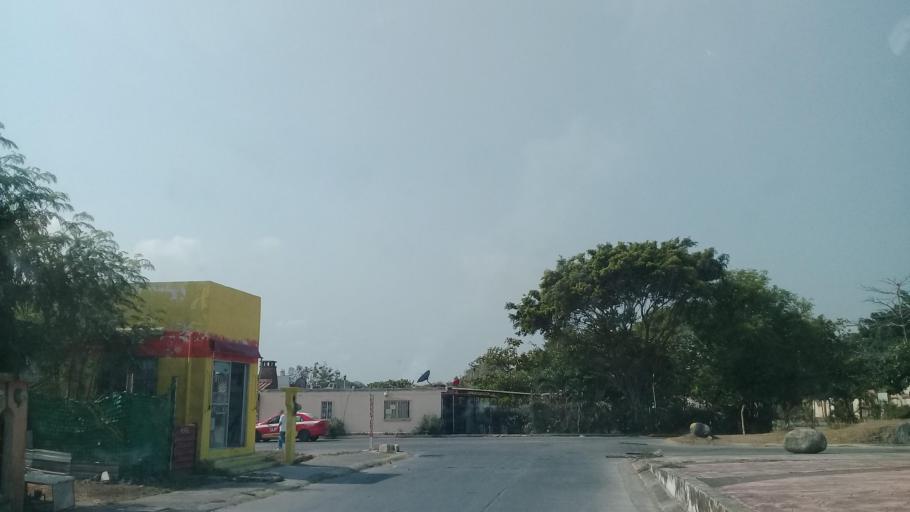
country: MX
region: Veracruz
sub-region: Veracruz
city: Hacienda Sotavento
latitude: 19.1298
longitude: -96.1801
